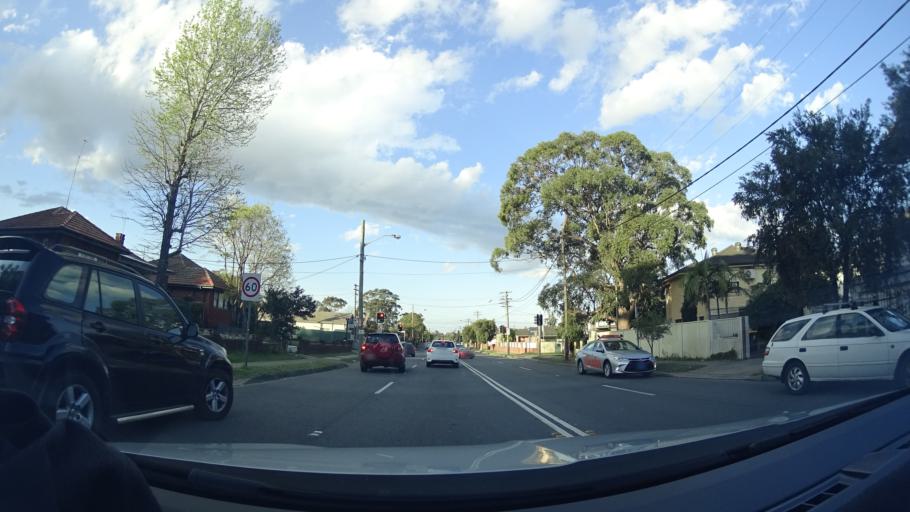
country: AU
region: New South Wales
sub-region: Canterbury
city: Roselands
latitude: -33.9240
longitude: 151.0570
